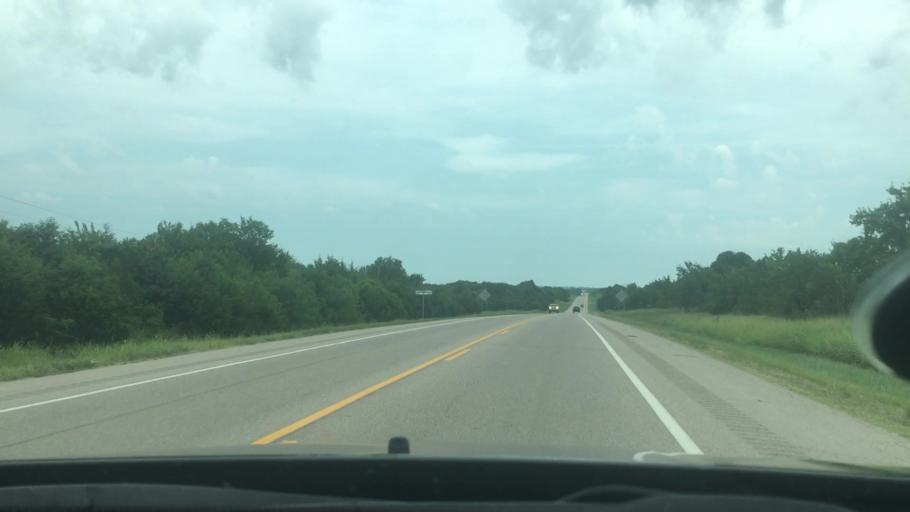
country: US
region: Oklahoma
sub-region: Seminole County
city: Konawa
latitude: 34.9859
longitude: -96.6793
